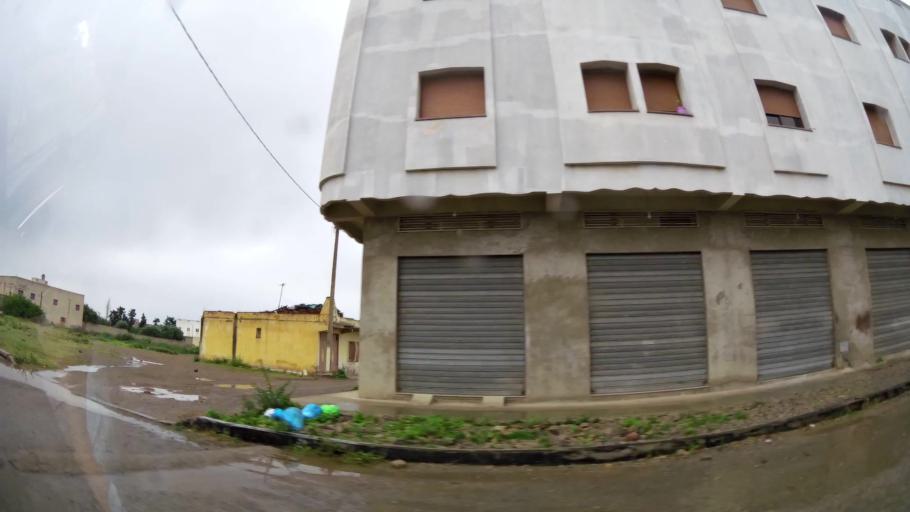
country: MA
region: Oriental
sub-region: Nador
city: Nador
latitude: 35.1550
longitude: -2.9617
